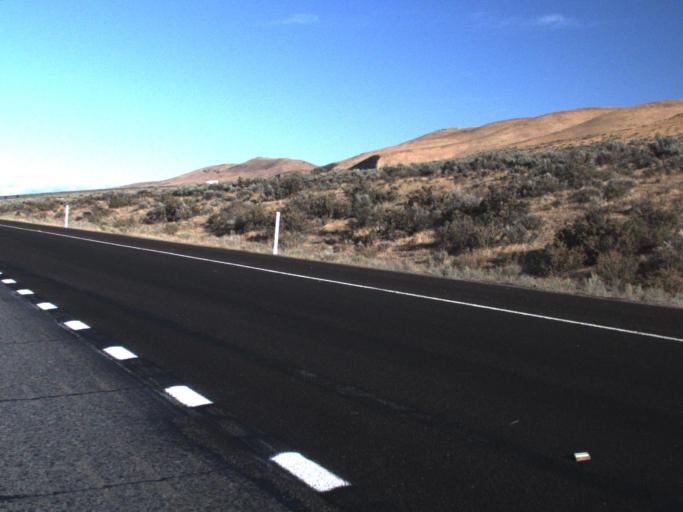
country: US
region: Washington
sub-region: Kittitas County
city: Kittitas
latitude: 46.8465
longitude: -120.3824
